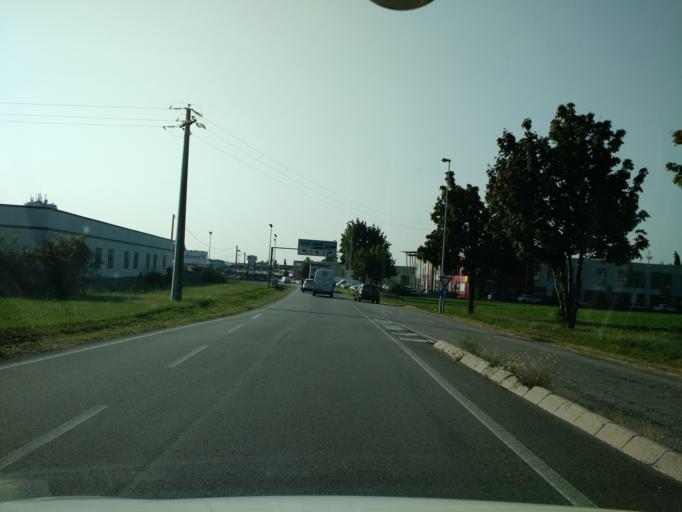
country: IT
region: Veneto
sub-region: Provincia di Vicenza
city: Thiene
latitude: 45.6919
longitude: 11.4809
